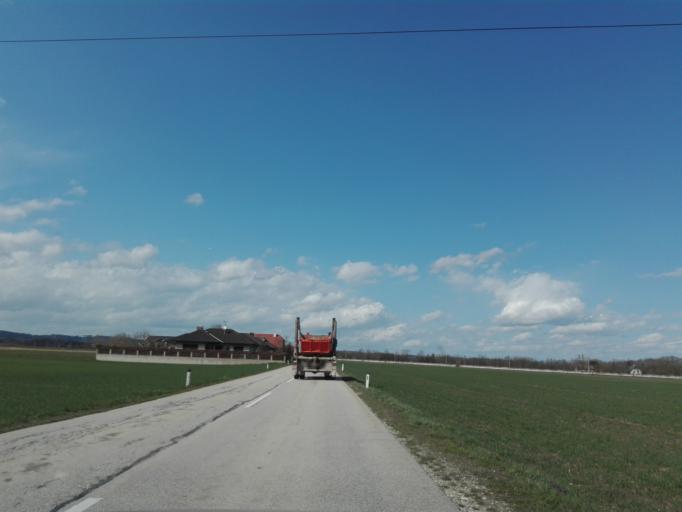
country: AT
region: Upper Austria
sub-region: Wels-Land
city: Marchtrenk
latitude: 48.2040
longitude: 14.1352
